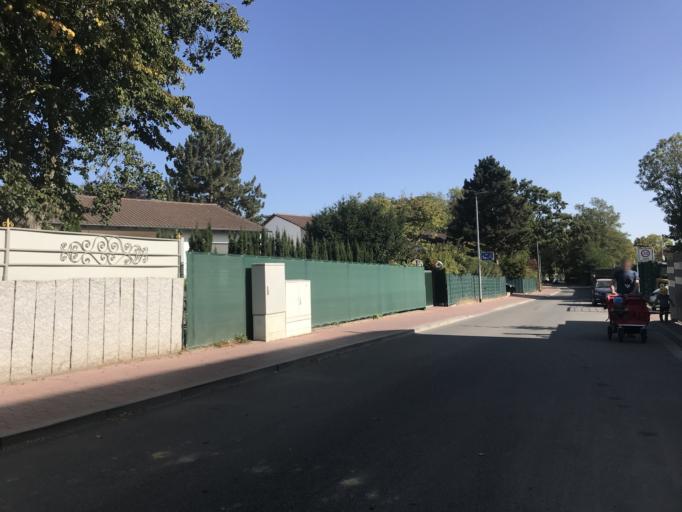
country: DE
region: Rheinland-Pfalz
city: Ober-Olm
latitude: 49.9538
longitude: 8.1941
